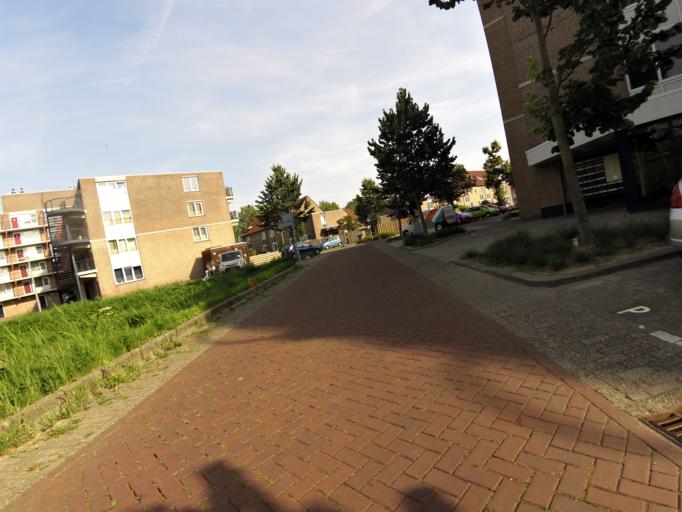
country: NL
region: South Holland
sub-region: Gemeente Papendrecht
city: Papendrecht
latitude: 51.8014
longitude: 4.7175
